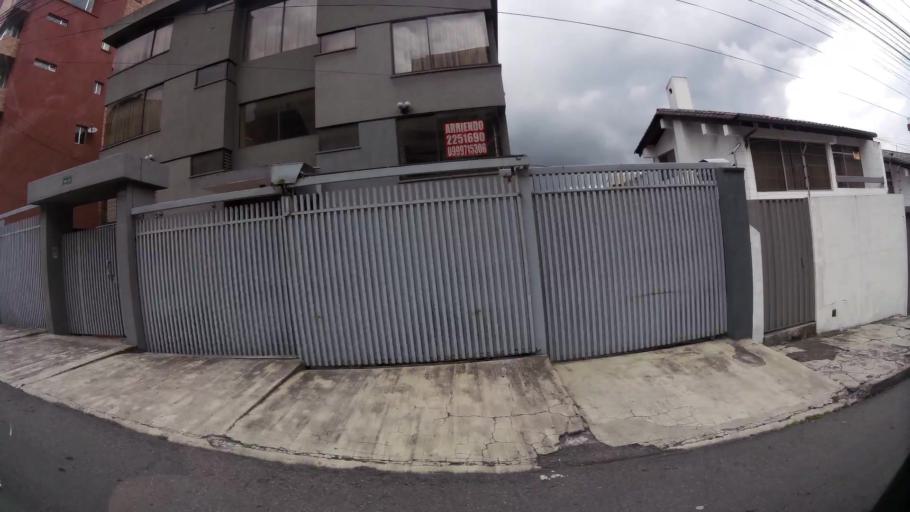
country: EC
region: Pichincha
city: Quito
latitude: -0.1669
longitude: -78.4961
